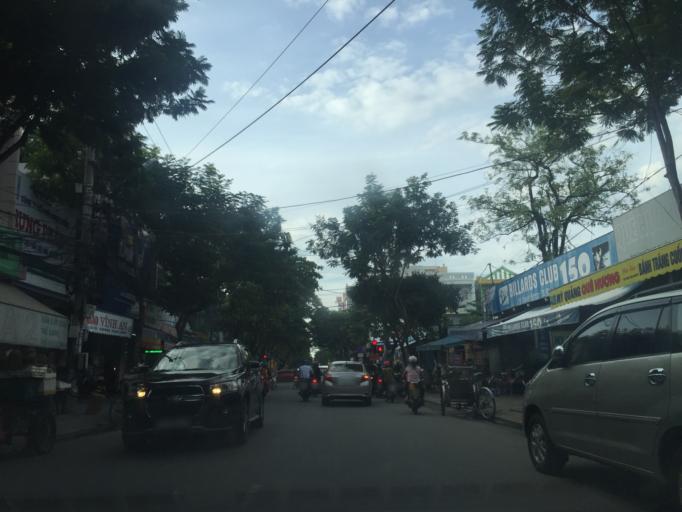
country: VN
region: Da Nang
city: Da Nang
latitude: 16.0739
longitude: 108.2127
